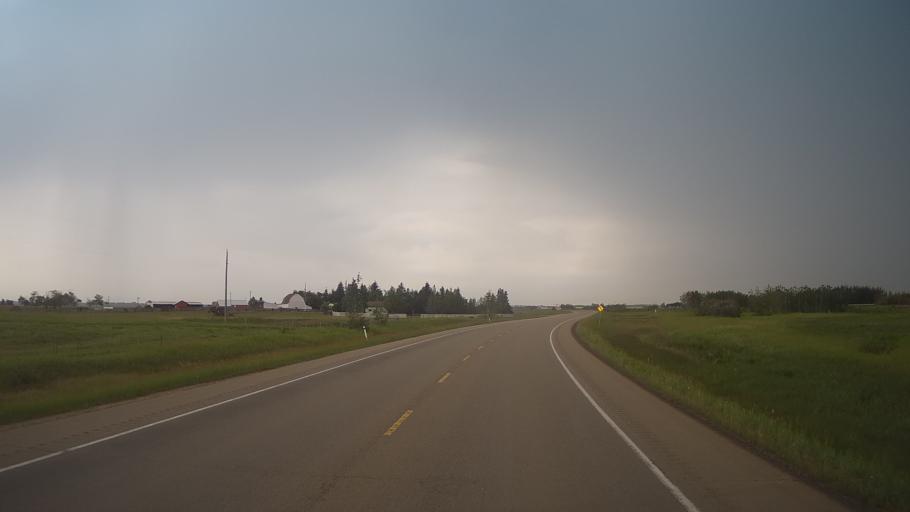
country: CA
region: Alberta
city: Tofield
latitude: 53.3293
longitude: -112.5735
